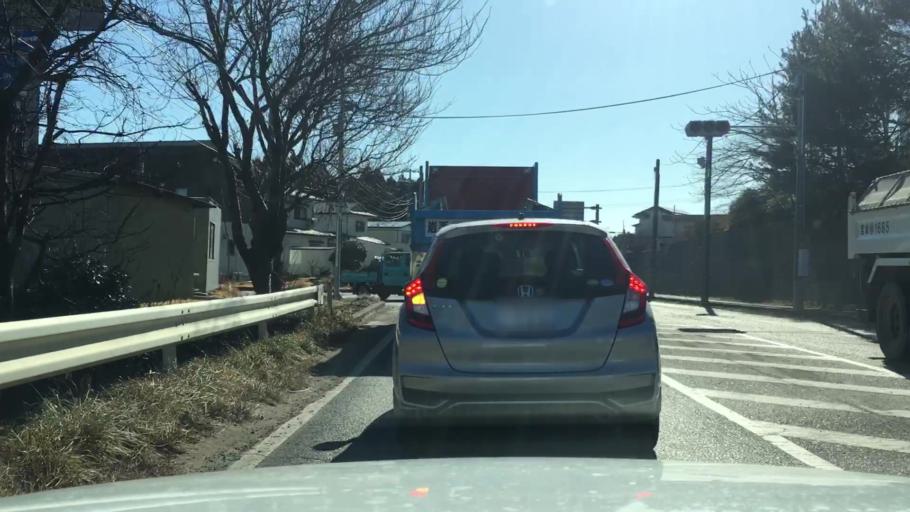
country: JP
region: Iwate
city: Yamada
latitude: 39.4389
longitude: 141.9725
